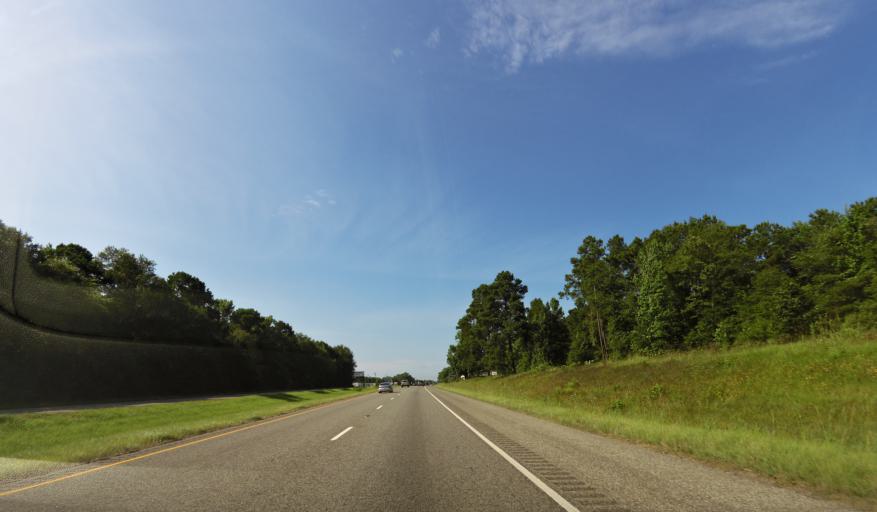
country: US
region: Texas
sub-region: Polk County
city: Corrigan
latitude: 31.0255
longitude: -94.8235
